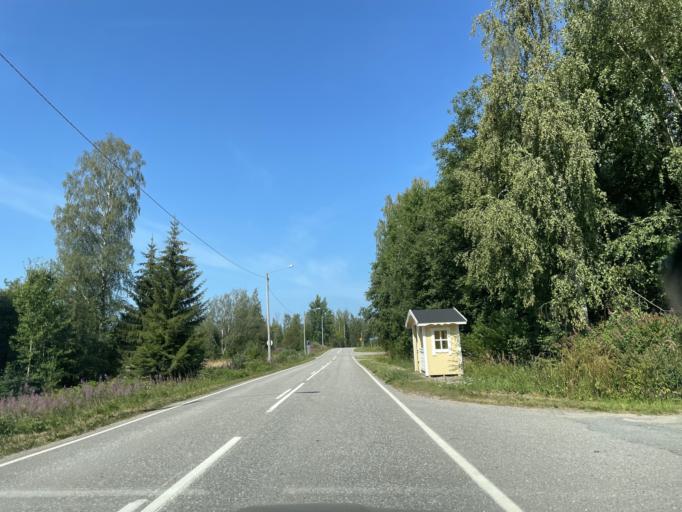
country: FI
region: Central Finland
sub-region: Saarijaervi-Viitasaari
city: Pihtipudas
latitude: 63.3577
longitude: 25.7530
